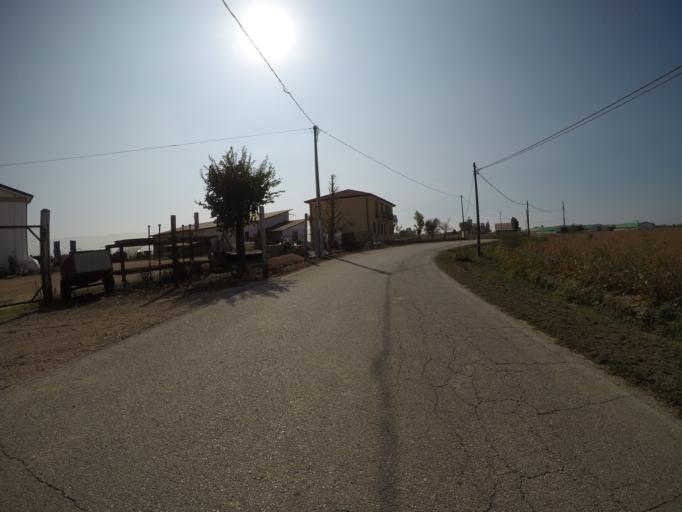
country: IT
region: Veneto
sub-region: Provincia di Rovigo
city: Polesella
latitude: 44.9727
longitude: 11.7230
